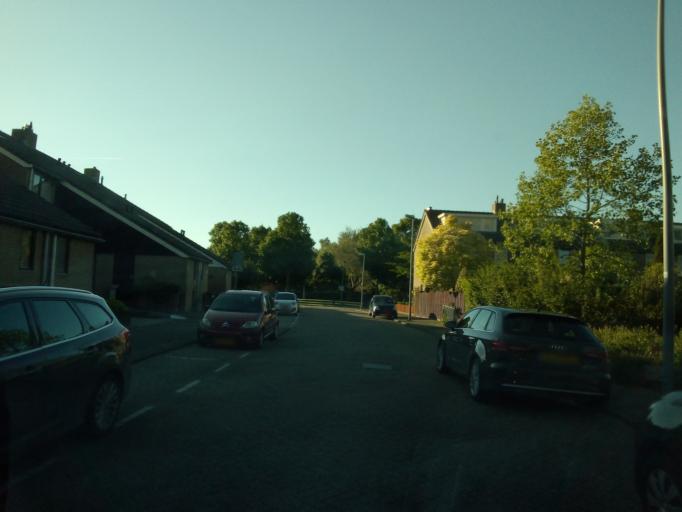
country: NL
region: South Holland
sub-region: Gemeente Lansingerland
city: Bergschenhoek
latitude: 51.9637
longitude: 4.5328
